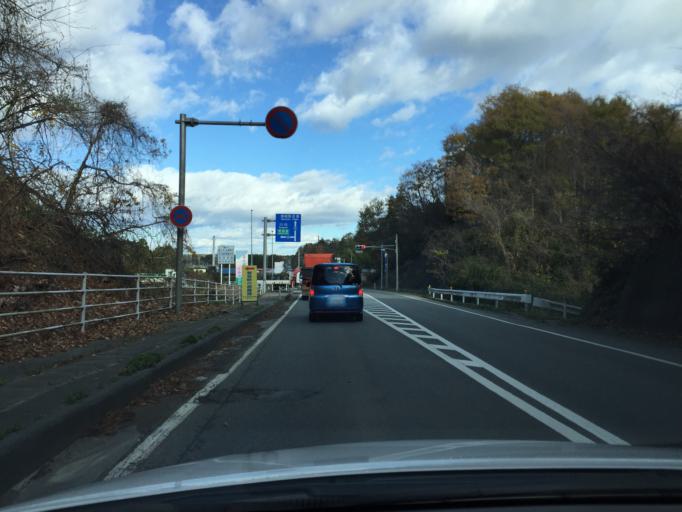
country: JP
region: Fukushima
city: Namie
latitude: 37.3708
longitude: 141.0091
